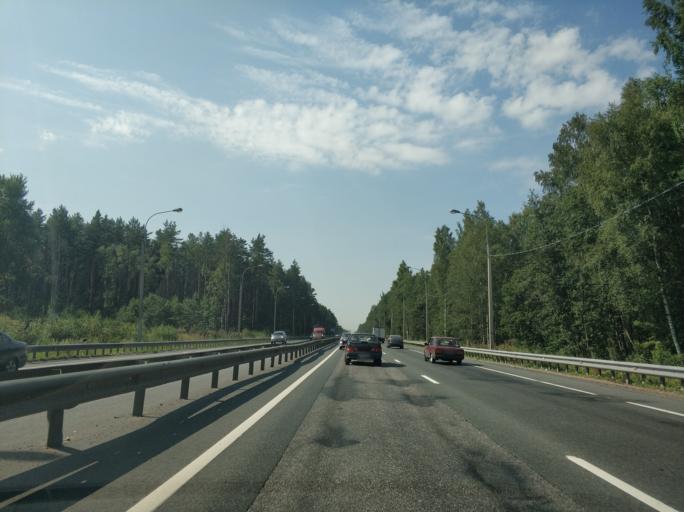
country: RU
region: St.-Petersburg
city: Krasnogvargeisky
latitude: 60.0008
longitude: 30.5542
